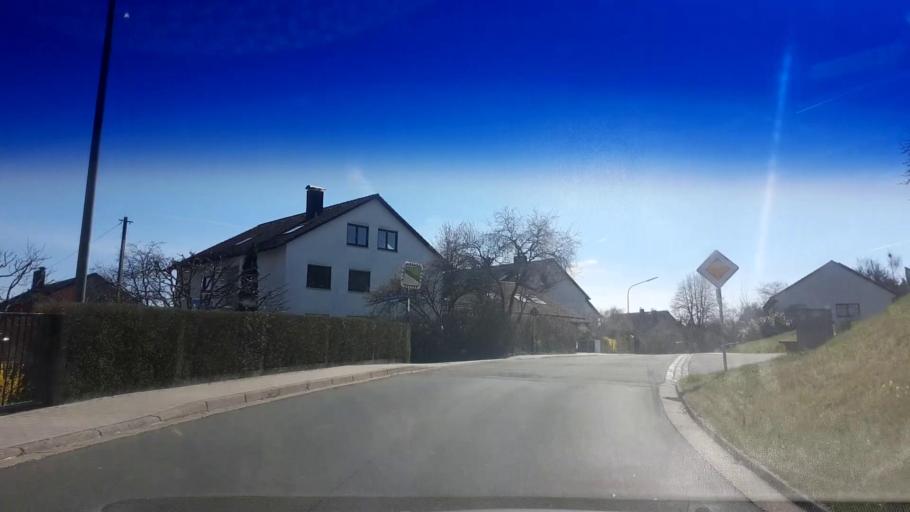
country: DE
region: Bavaria
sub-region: Upper Franconia
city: Bindlach
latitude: 50.0105
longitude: 11.6252
